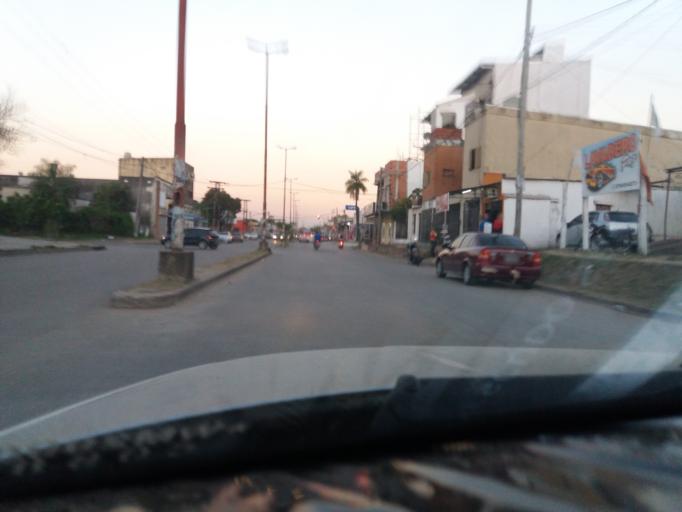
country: AR
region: Corrientes
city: Corrientes
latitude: -27.4851
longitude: -58.8407
